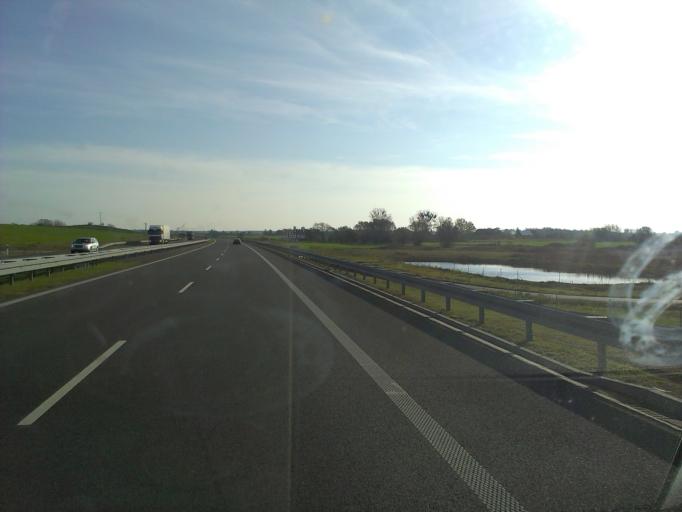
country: PL
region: West Pomeranian Voivodeship
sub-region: Powiat pyrzycki
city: Lipiany
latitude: 52.9585
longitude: 14.9306
